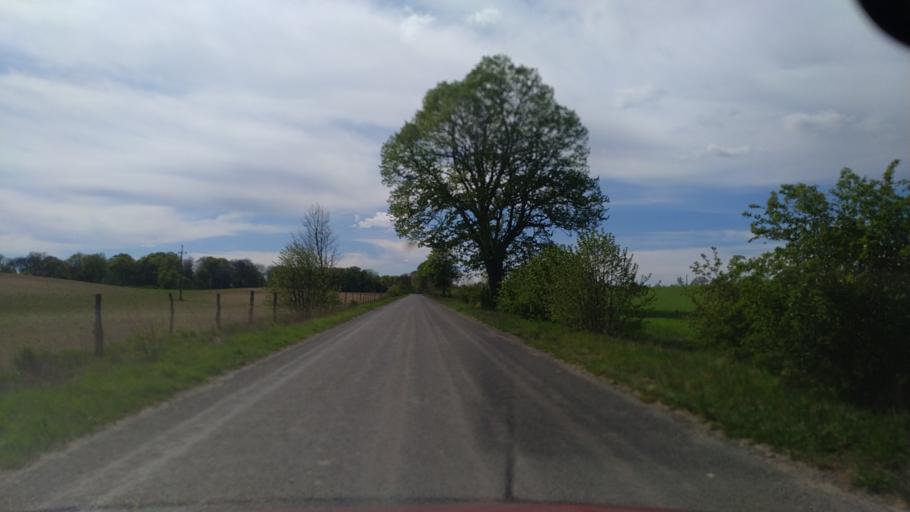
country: PL
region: West Pomeranian Voivodeship
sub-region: Powiat walecki
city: Walcz
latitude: 53.3541
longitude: 16.2978
